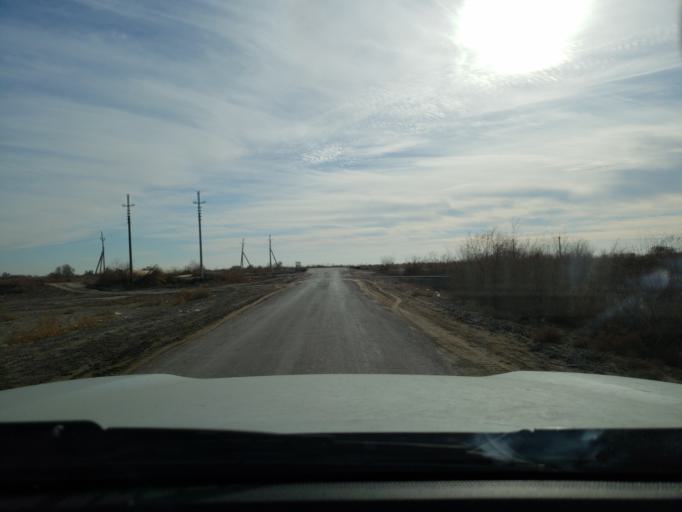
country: TM
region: Dasoguz
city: Dasoguz
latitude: 41.8503
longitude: 59.8870
